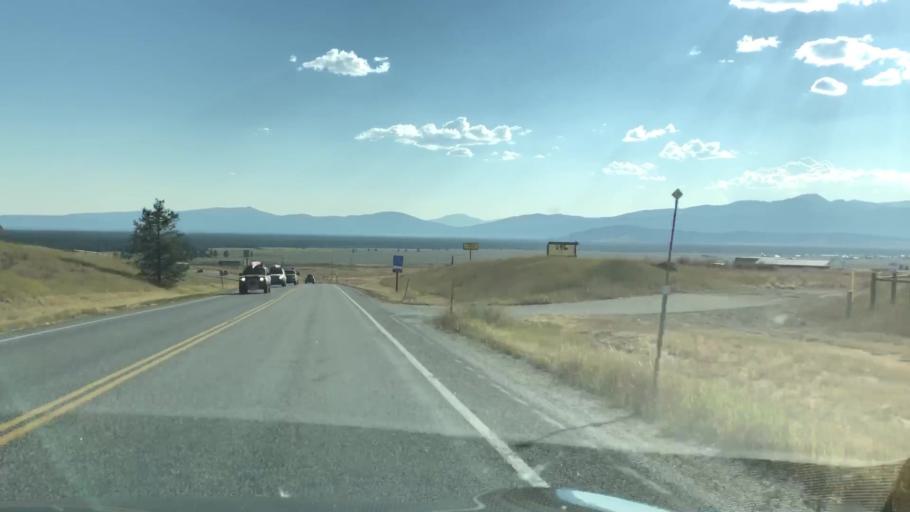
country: US
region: Montana
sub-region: Gallatin County
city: West Yellowstone
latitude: 44.7911
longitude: -111.1101
